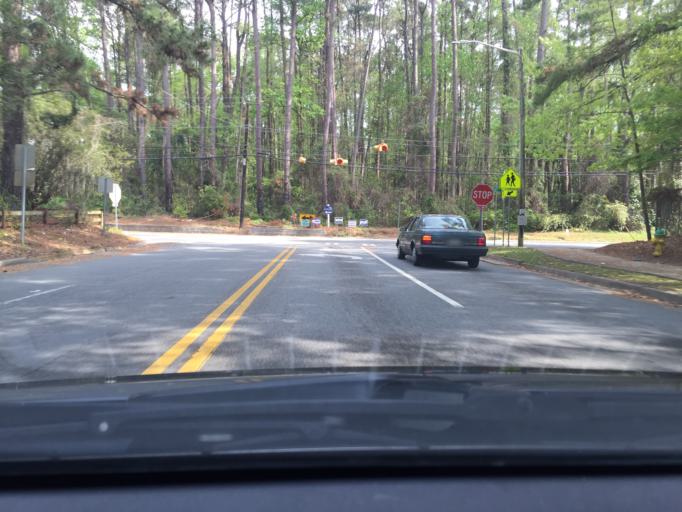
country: US
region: Georgia
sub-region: Chatham County
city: Montgomery
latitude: 31.9931
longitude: -81.1435
